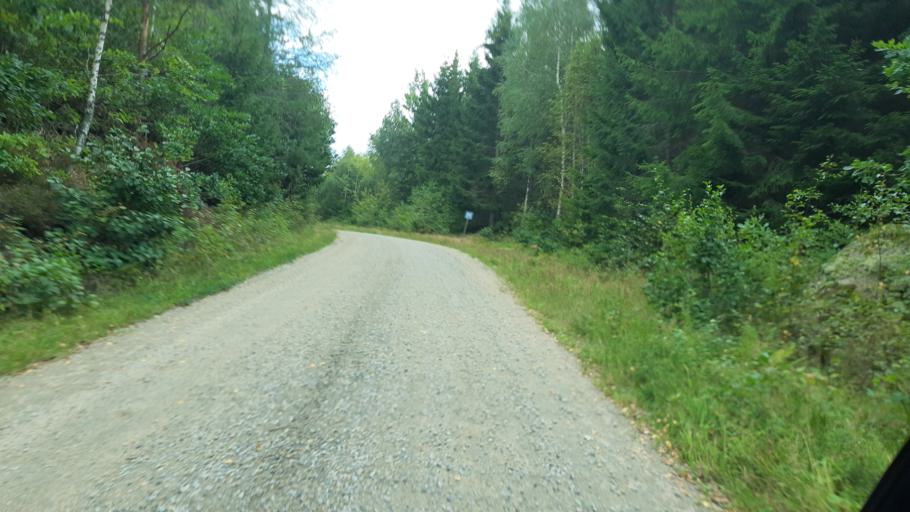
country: SE
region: Blekinge
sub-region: Ronneby Kommun
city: Brakne-Hoby
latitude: 56.4248
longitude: 15.1859
